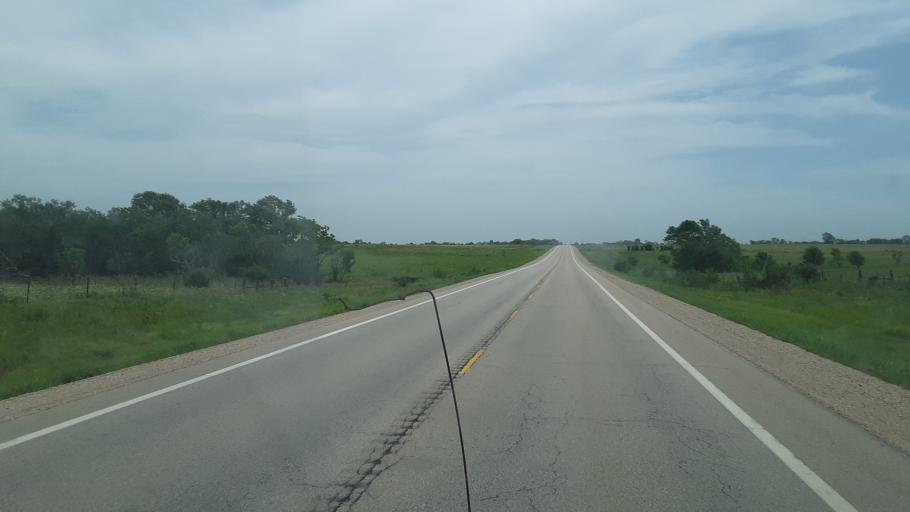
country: US
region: Kansas
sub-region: Woodson County
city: Yates Center
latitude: 37.8363
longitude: -95.8947
